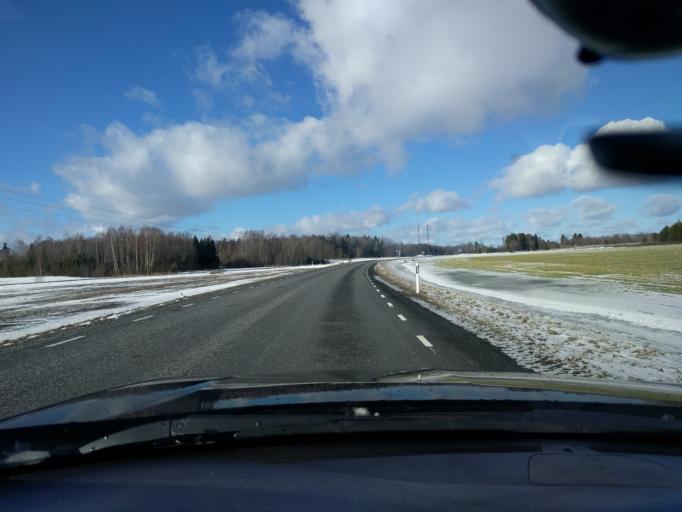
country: EE
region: Harju
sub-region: Anija vald
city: Kehra
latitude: 59.2528
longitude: 25.3303
